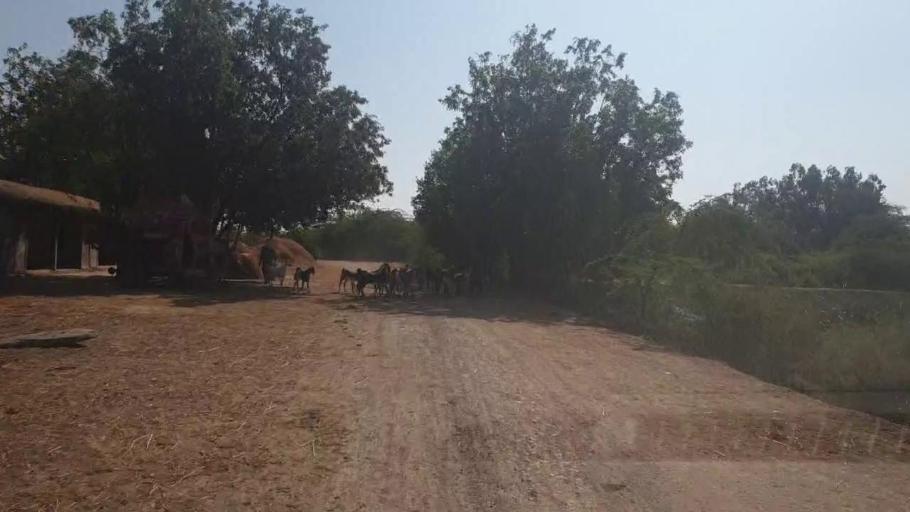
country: PK
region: Sindh
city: Badin
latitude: 24.5465
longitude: 68.8445
